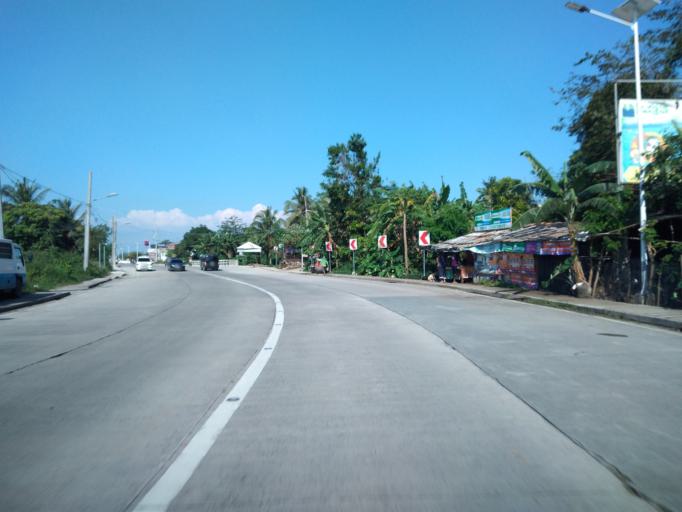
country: PH
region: Calabarzon
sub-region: Province of Laguna
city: Prinza
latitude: 14.1797
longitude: 121.1581
